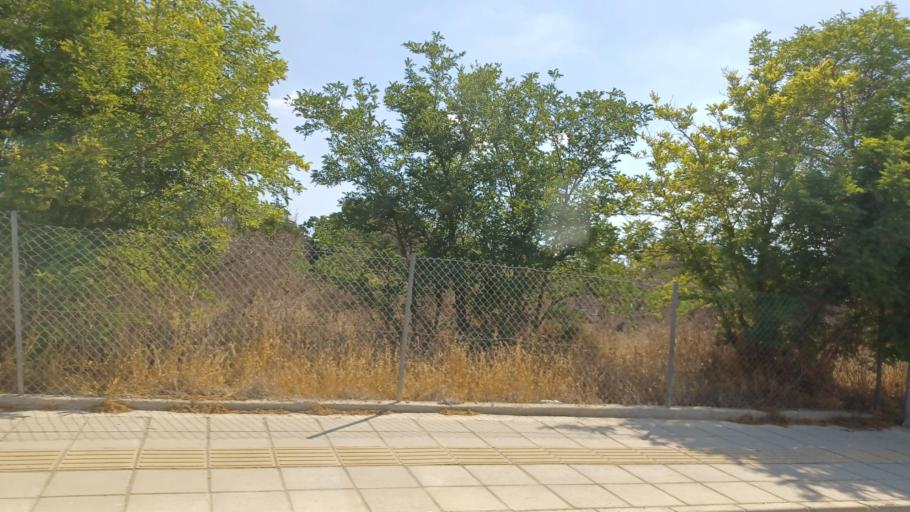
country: CY
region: Ammochostos
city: Acheritou
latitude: 35.0803
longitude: 33.8739
